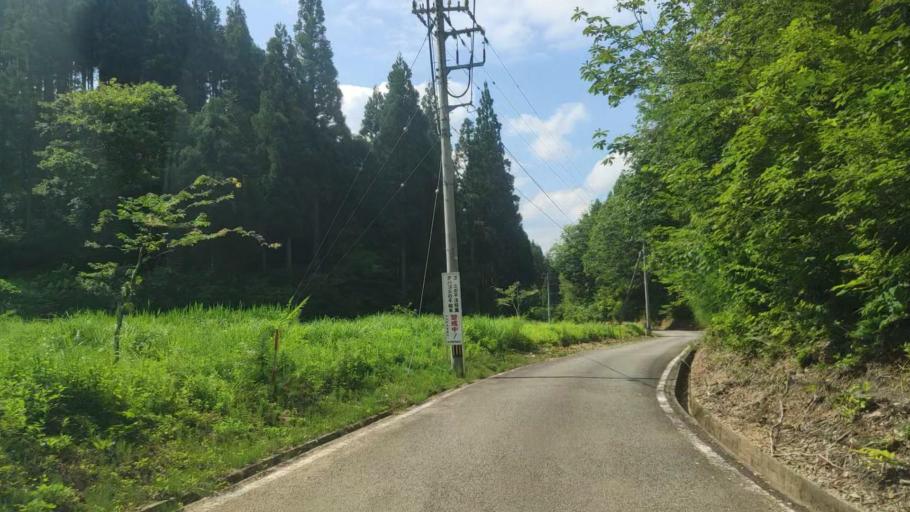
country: JP
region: Ishikawa
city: Komatsu
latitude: 36.2726
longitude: 136.5346
